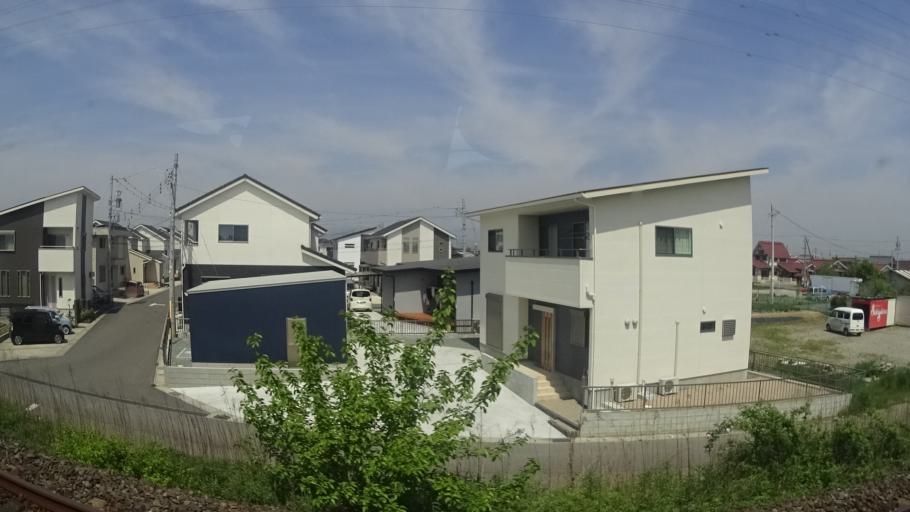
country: JP
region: Mie
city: Suzuka
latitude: 34.8654
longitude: 136.5794
